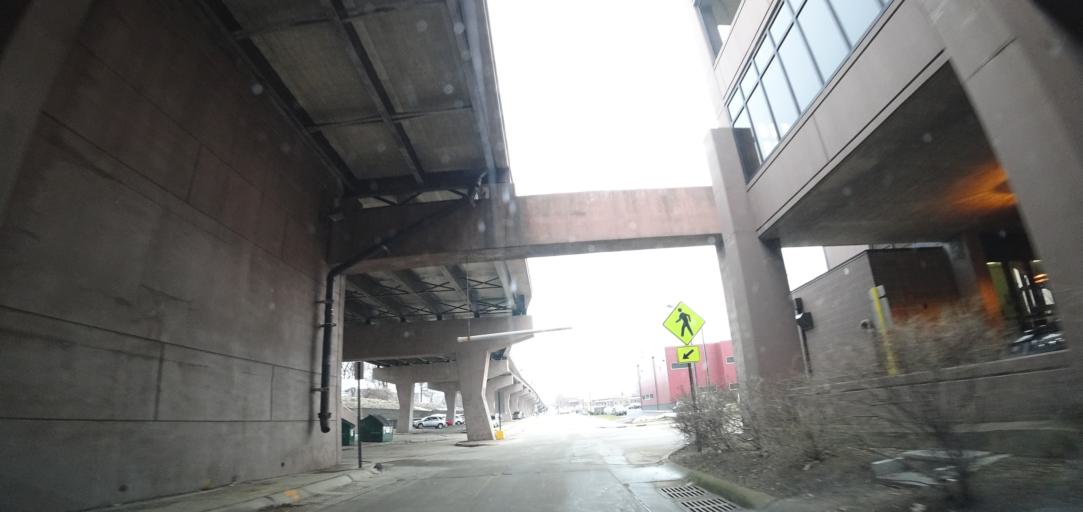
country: US
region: Ohio
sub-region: Summit County
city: Akron
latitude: 41.0710
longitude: -81.5243
